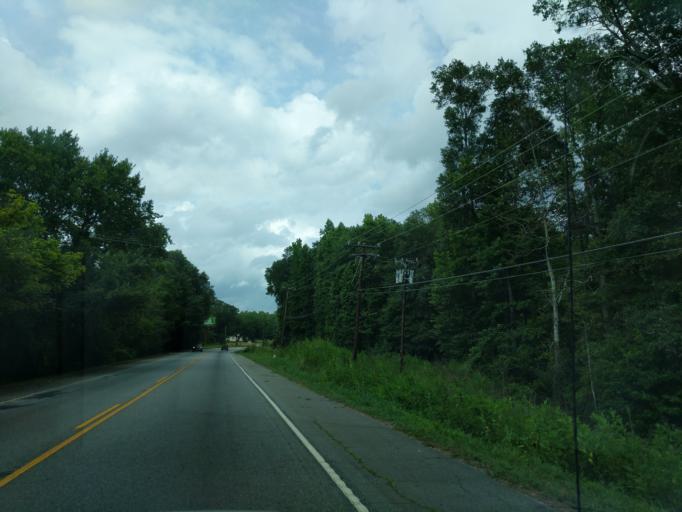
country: US
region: South Carolina
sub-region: Anderson County
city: Anderson
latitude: 34.5102
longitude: -82.6018
